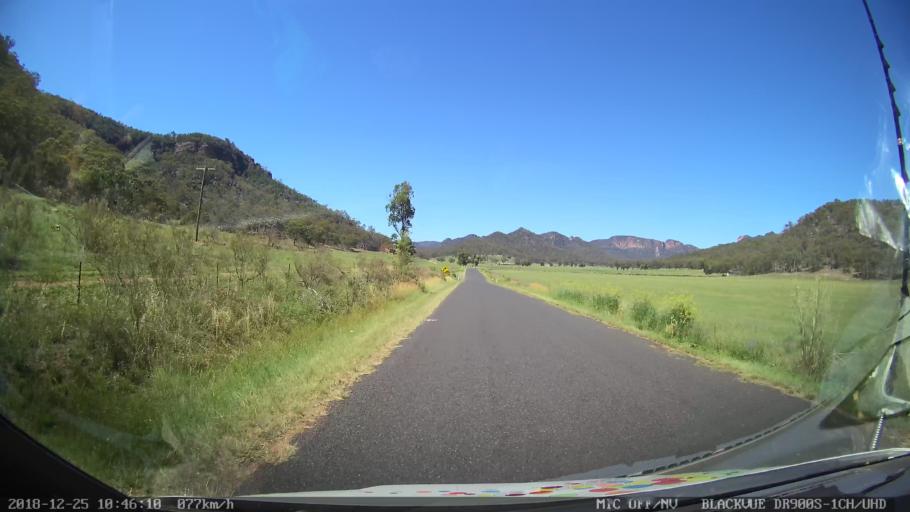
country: AU
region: New South Wales
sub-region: Upper Hunter Shire
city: Merriwa
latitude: -32.4412
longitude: 150.2865
